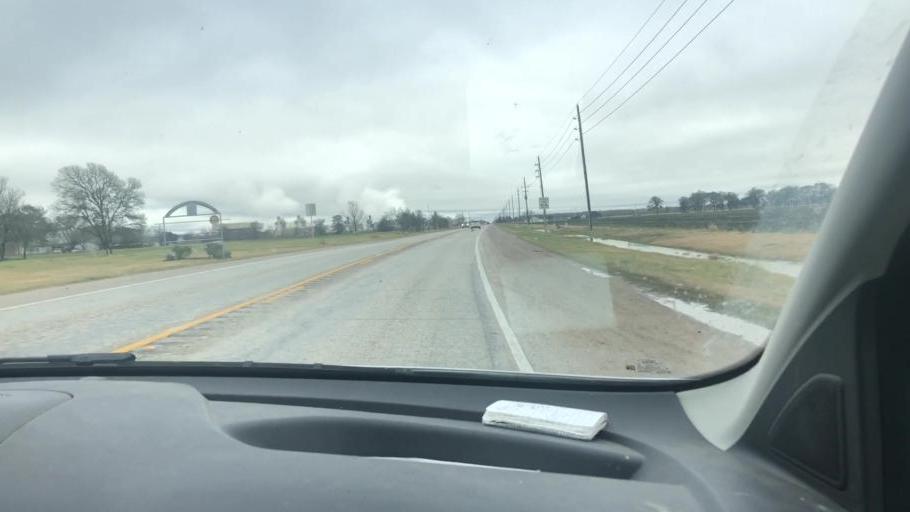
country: US
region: Texas
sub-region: Wharton County
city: Wharton
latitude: 29.3031
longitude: -96.0799
